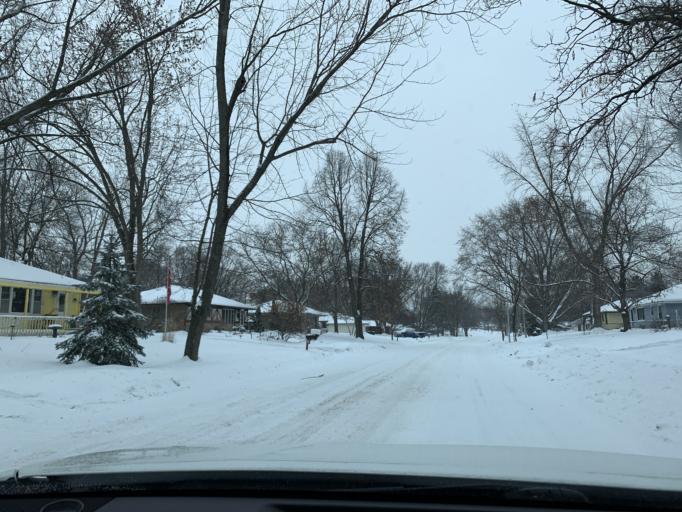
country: US
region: Minnesota
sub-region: Anoka County
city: Coon Rapids
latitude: 45.1733
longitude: -93.2872
